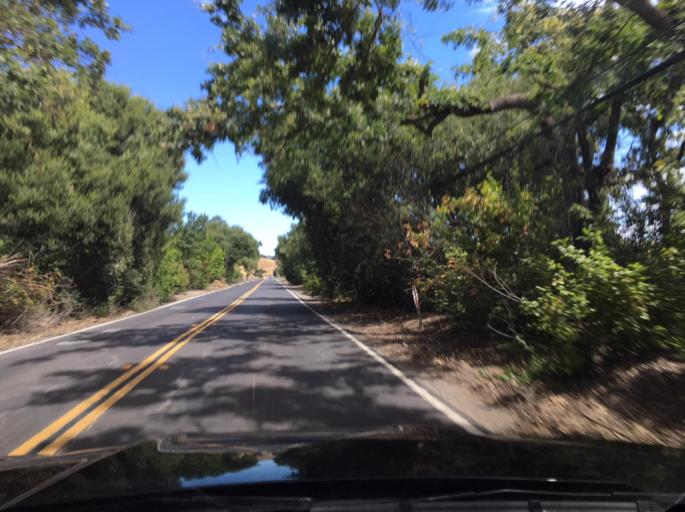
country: US
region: California
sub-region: Santa Clara County
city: Morgan Hill
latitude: 37.1738
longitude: -121.7592
